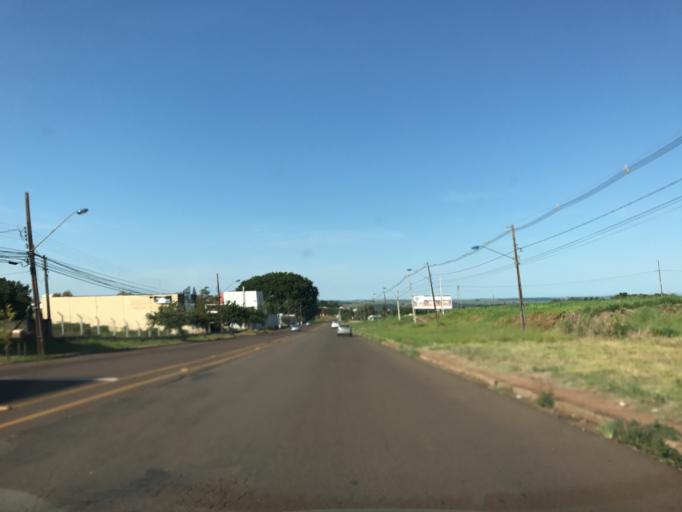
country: BR
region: Parana
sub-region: Maringa
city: Maringa
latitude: -23.4532
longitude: -51.9535
